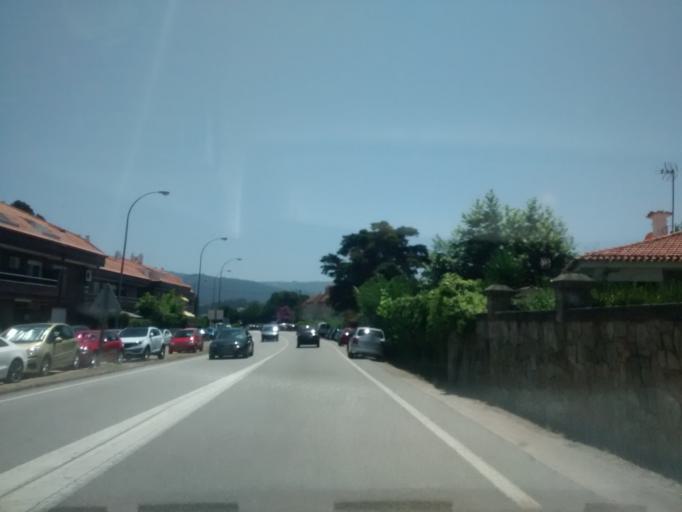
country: ES
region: Galicia
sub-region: Provincia de Pontevedra
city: Nigran
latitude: 42.1239
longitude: -8.8195
